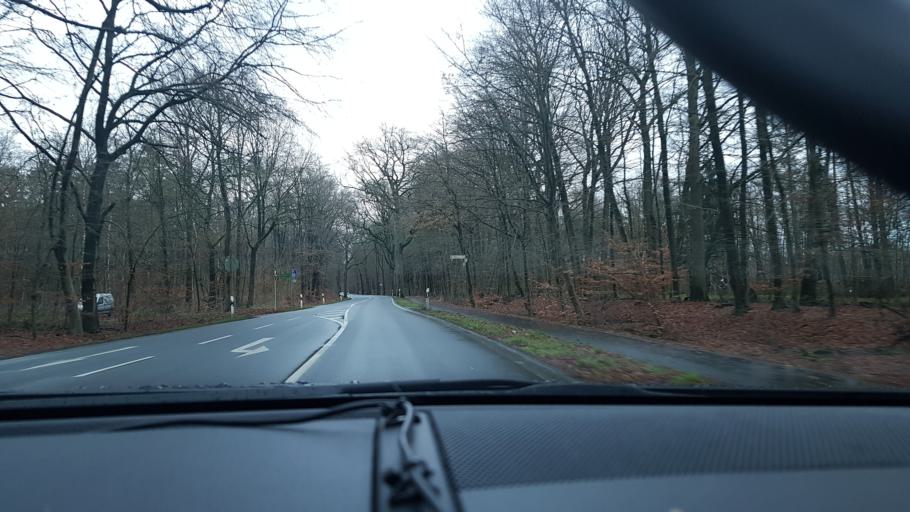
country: NL
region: Limburg
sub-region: Gemeente Beesel
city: Offenbeek
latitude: 51.2336
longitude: 6.1154
